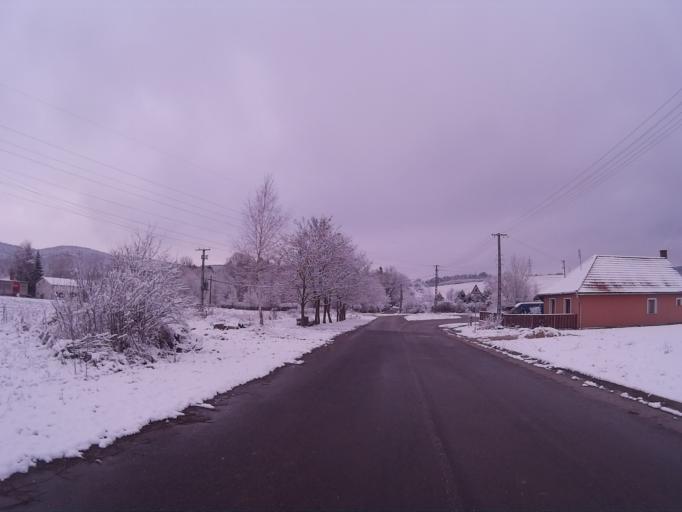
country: HU
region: Fejer
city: Szarliget
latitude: 47.5211
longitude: 18.5436
